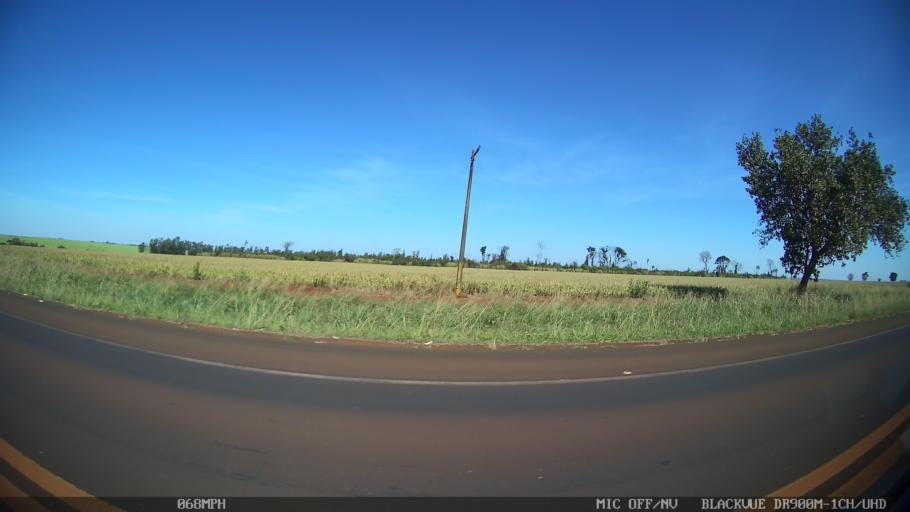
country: BR
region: Sao Paulo
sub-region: Guaira
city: Guaira
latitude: -20.4454
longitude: -48.3938
